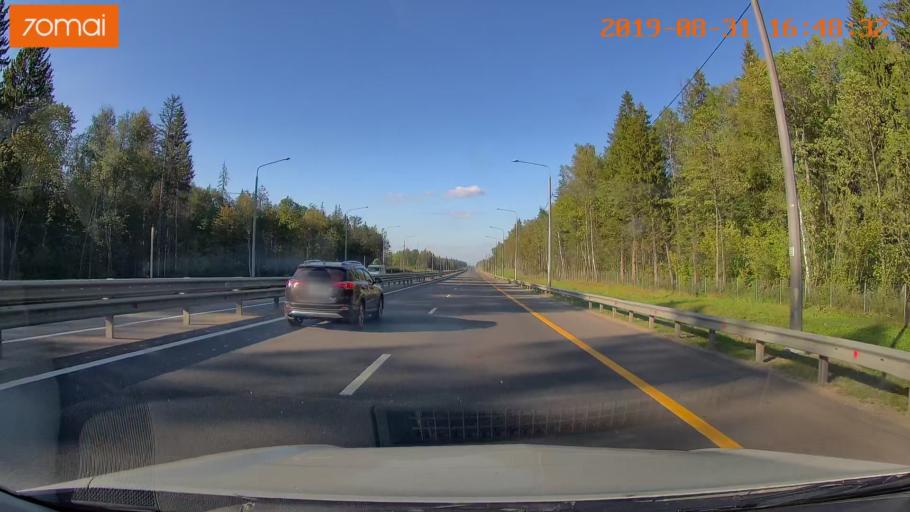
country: RU
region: Kaluga
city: Pyatovskiy
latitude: 54.6738
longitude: 36.1475
